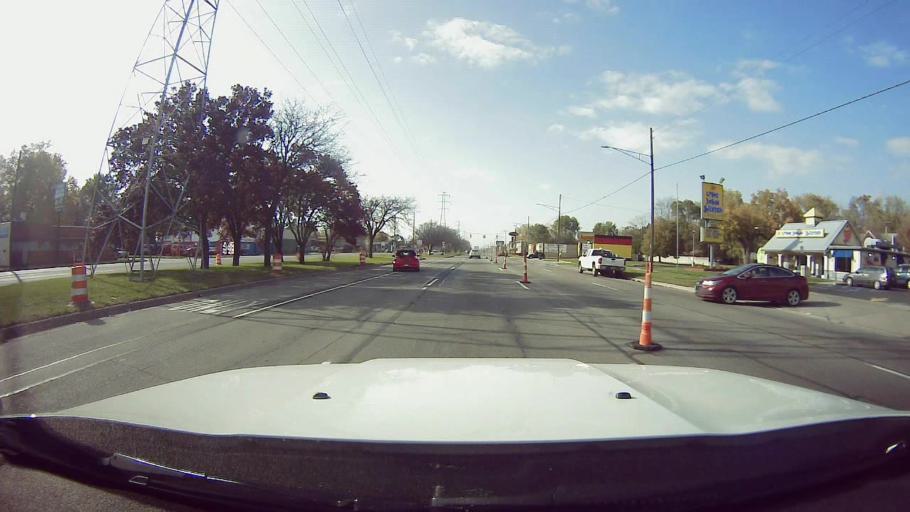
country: US
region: Michigan
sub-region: Oakland County
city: Hazel Park
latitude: 42.4475
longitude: -83.0673
